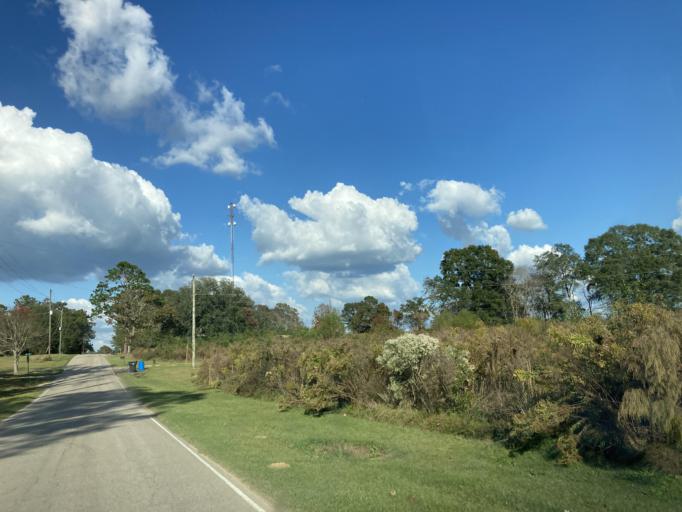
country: US
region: Mississippi
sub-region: Lamar County
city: Sumrall
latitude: 31.4276
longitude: -89.6392
